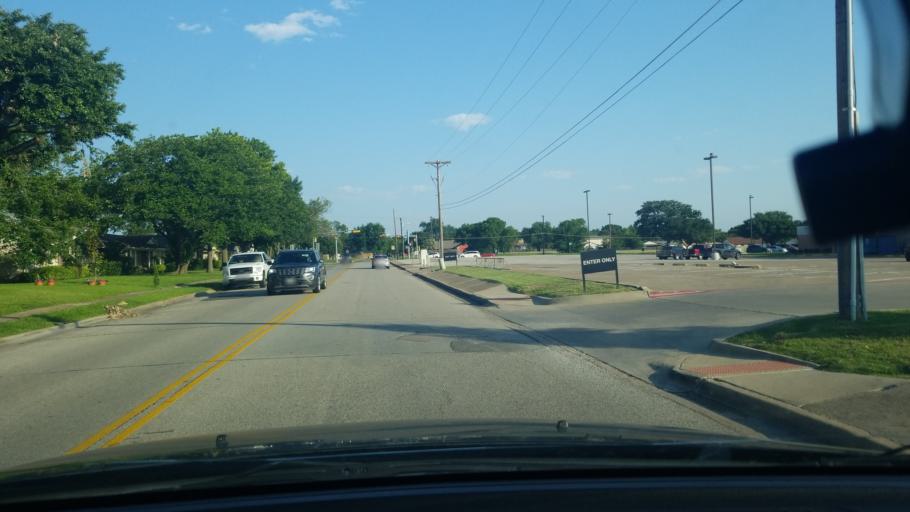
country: US
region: Texas
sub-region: Dallas County
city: Mesquite
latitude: 32.8037
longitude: -96.6411
